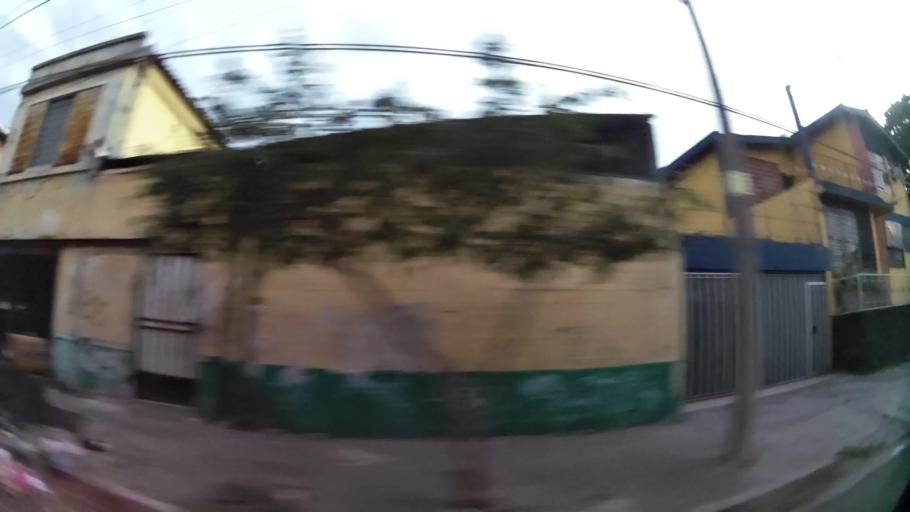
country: SV
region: San Salvador
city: Delgado
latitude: 13.7122
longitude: -89.1882
